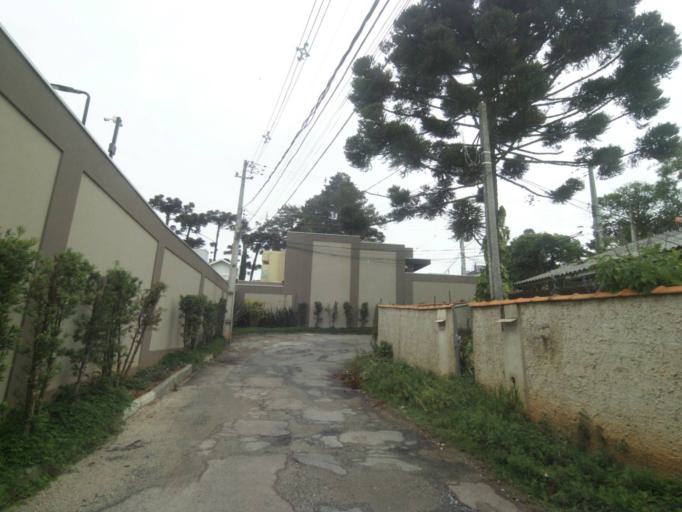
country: BR
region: Parana
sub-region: Curitiba
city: Curitiba
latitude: -25.4286
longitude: -49.3336
